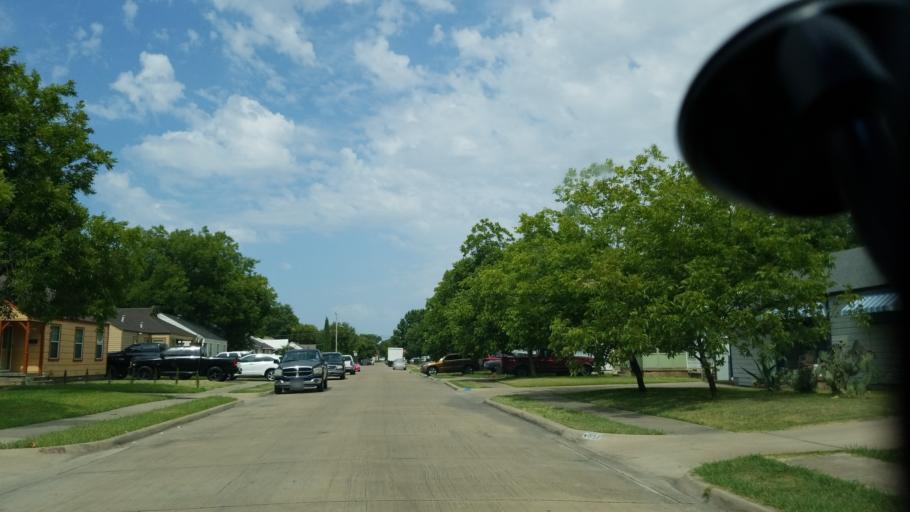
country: US
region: Texas
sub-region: Dallas County
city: Grand Prairie
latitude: 32.7504
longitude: -96.9827
